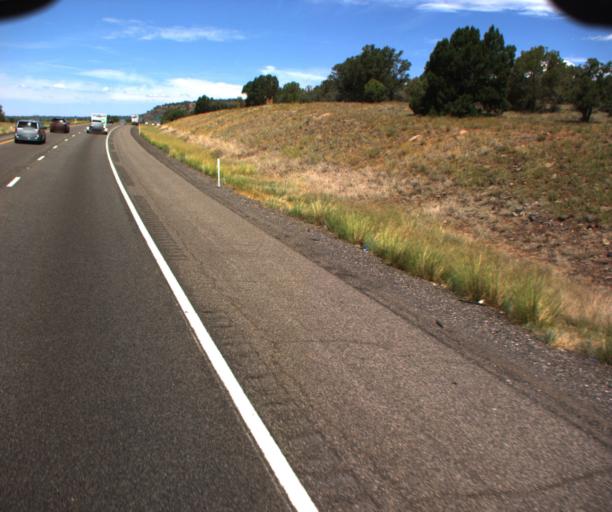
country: US
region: Arizona
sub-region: Yavapai County
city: Village of Oak Creek (Big Park)
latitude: 34.8008
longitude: -111.5938
